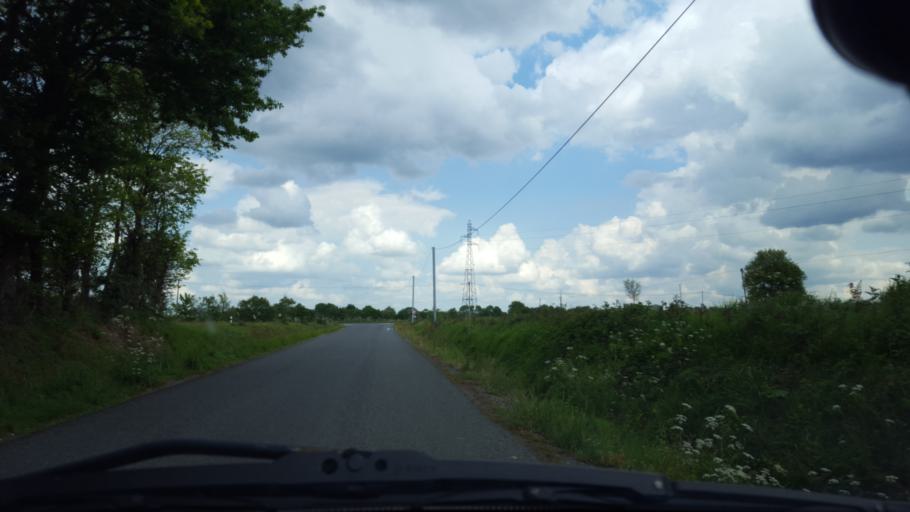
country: FR
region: Pays de la Loire
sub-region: Departement de la Loire-Atlantique
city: Saint-Philbert-de-Grand-Lieu
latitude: 47.0384
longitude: -1.6012
